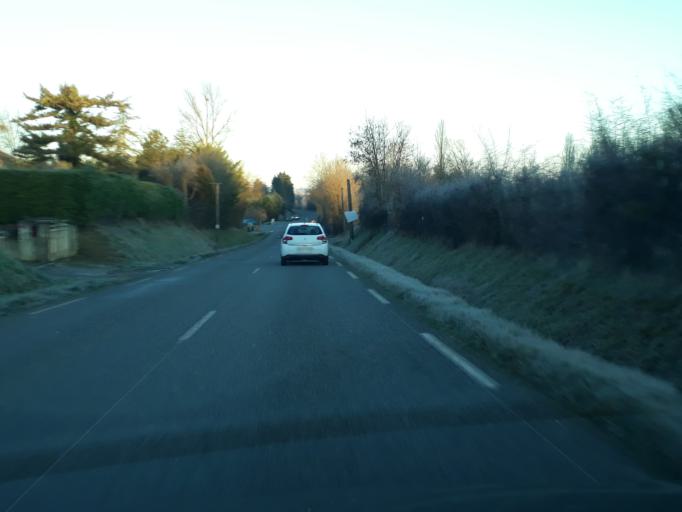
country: FR
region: Midi-Pyrenees
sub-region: Departement du Gers
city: Pavie
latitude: 43.6331
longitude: 0.6111
